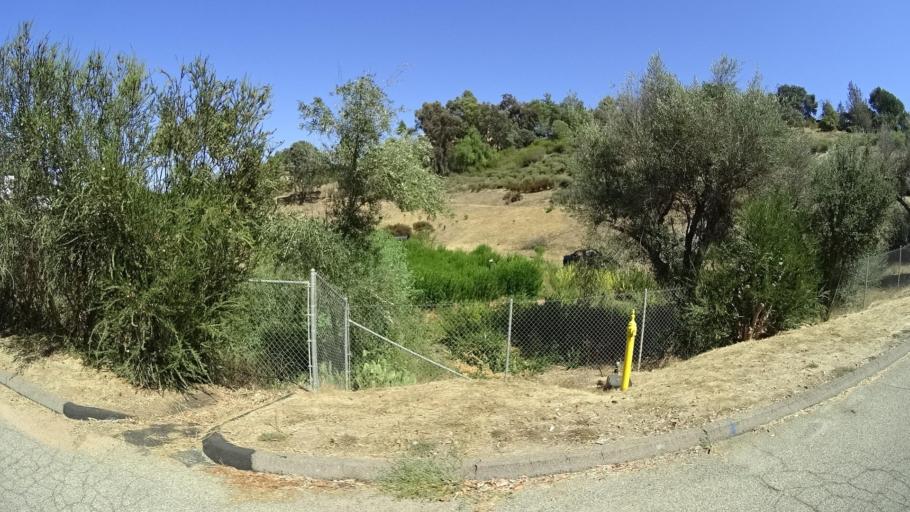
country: US
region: California
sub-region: San Diego County
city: Bonsall
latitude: 33.2871
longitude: -117.1959
